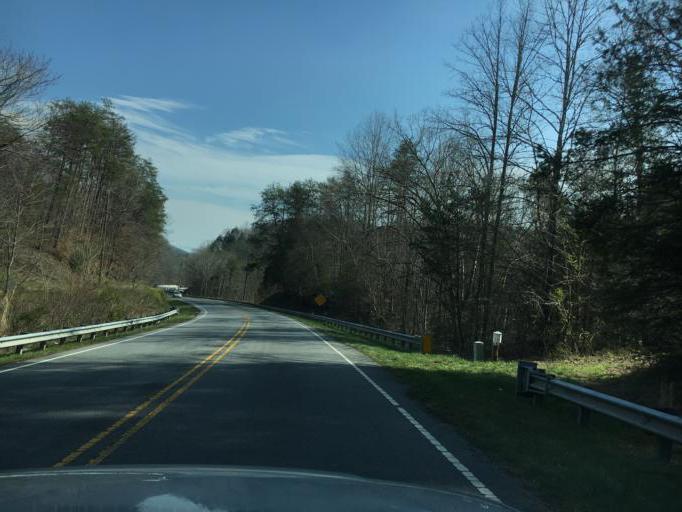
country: US
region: North Carolina
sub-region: McDowell County
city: West Marion
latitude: 35.5788
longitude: -81.9794
